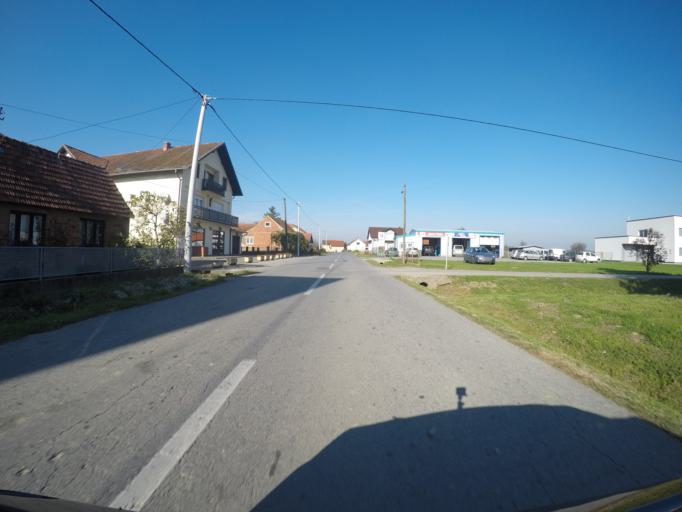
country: HR
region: Bjelovarsko-Bilogorska
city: Gudovac
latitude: 45.9037
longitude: 16.7716
